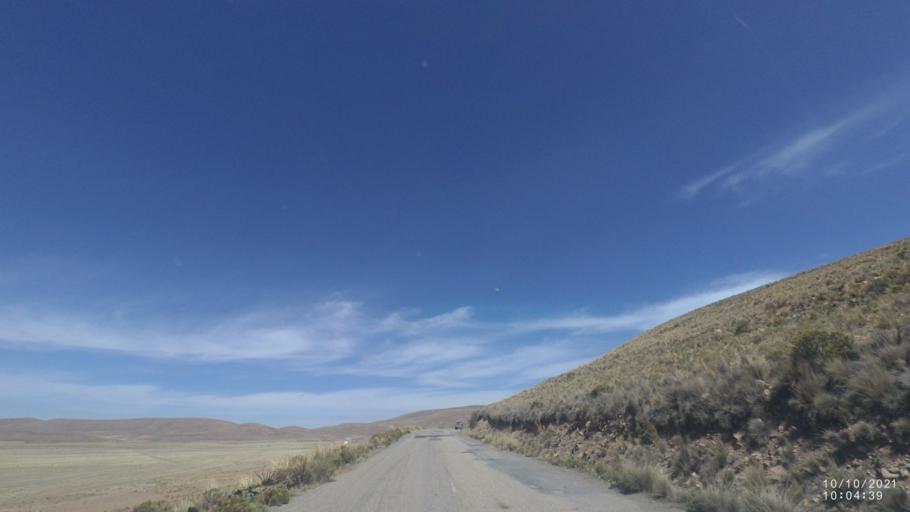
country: BO
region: La Paz
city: Eucaliptus
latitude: -17.3823
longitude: -67.4489
